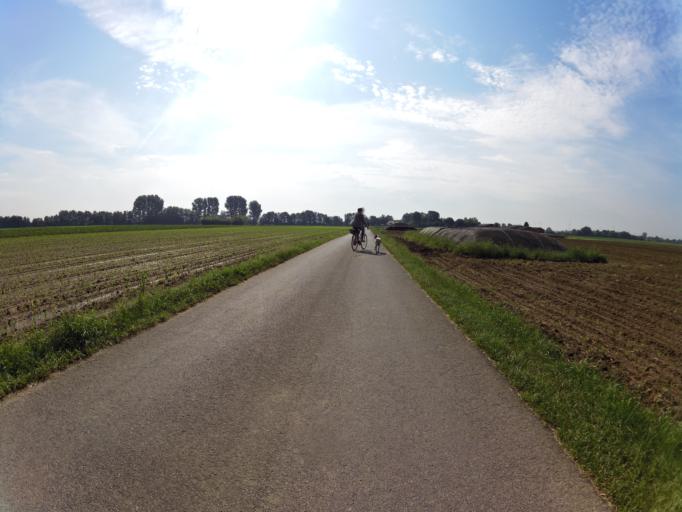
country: DE
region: North Rhine-Westphalia
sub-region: Regierungsbezirk Koln
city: Waldfeucht
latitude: 51.0718
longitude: 6.0003
